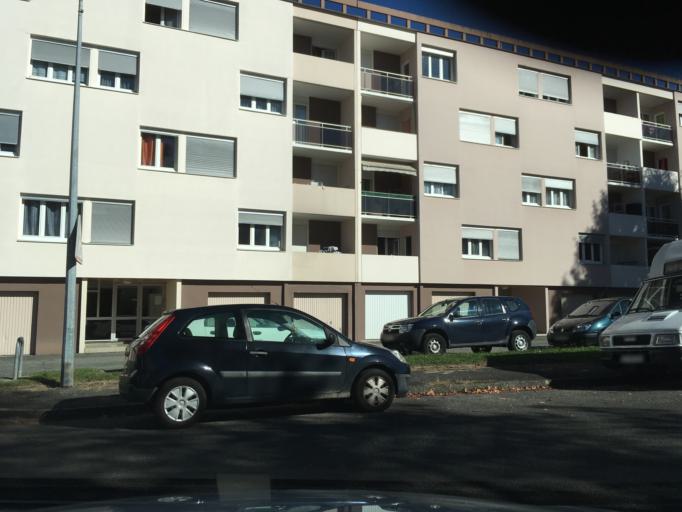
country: FR
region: Aquitaine
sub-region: Departement des Pyrenees-Atlantiques
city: Pau
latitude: 43.3156
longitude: -0.3442
